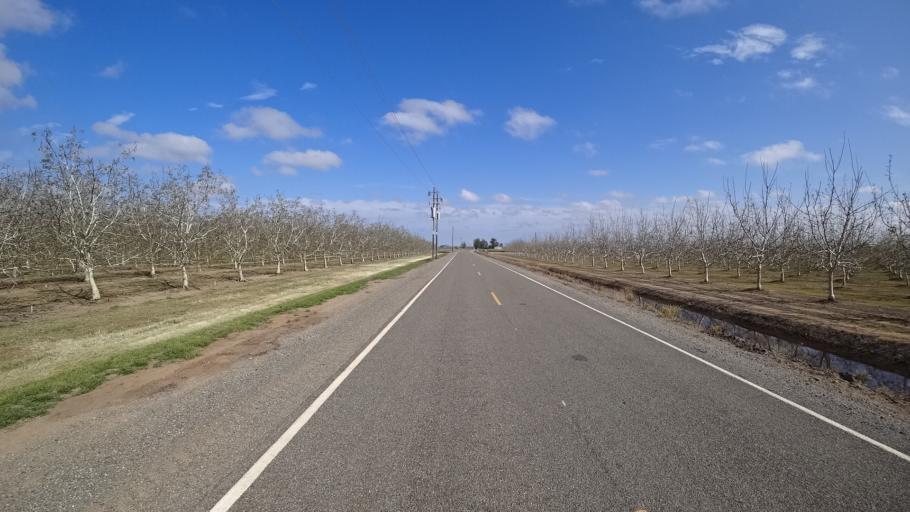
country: US
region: California
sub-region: Butte County
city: Biggs
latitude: 39.4478
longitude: -121.9303
